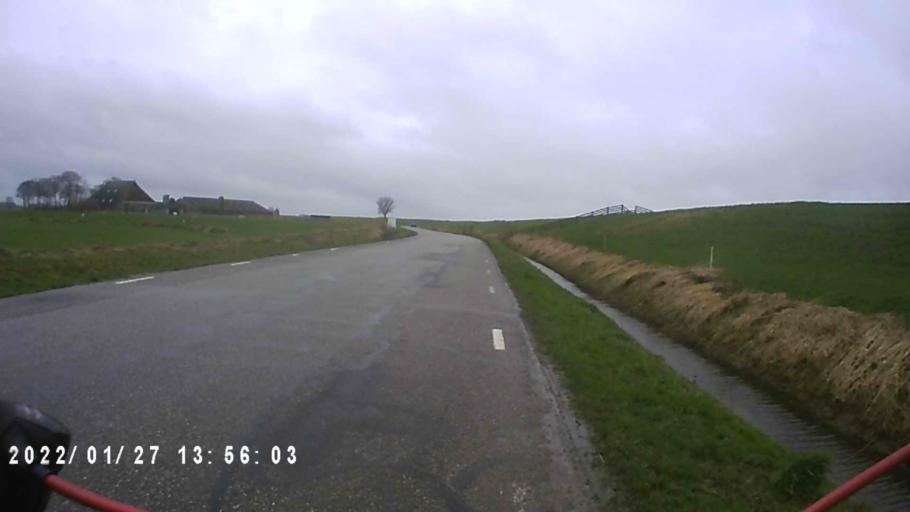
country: NL
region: Friesland
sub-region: Gemeente Kollumerland en Nieuwkruisland
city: Kollum
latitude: 53.3075
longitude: 6.1827
